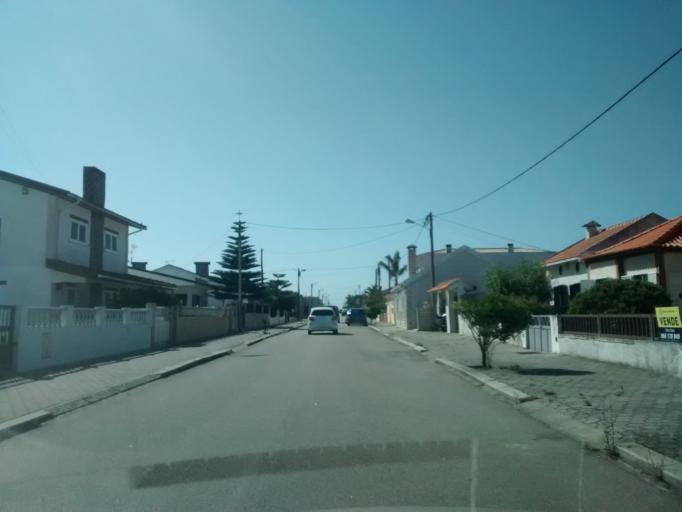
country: PT
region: Aveiro
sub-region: Ilhavo
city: Gafanha da Nazare
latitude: 40.6647
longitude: -8.7319
